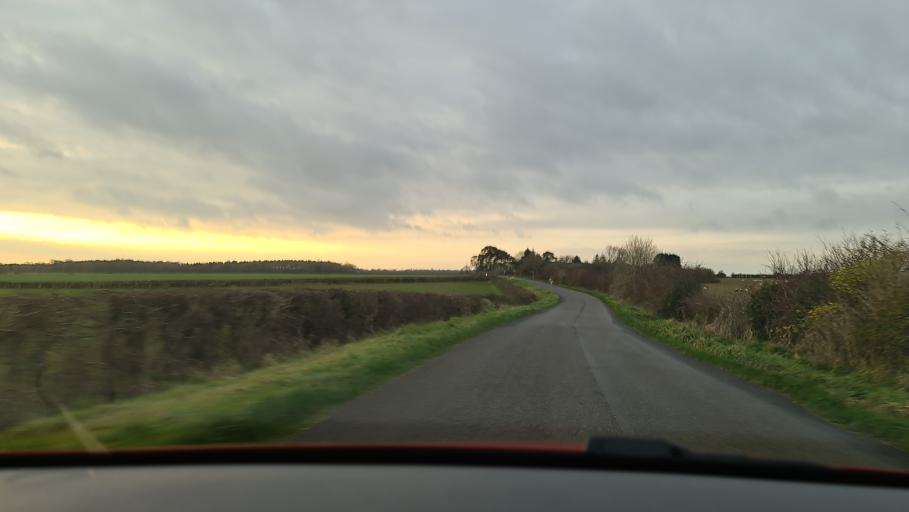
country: GB
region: England
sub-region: Oxfordshire
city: Somerton
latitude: 51.9114
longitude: -1.2753
